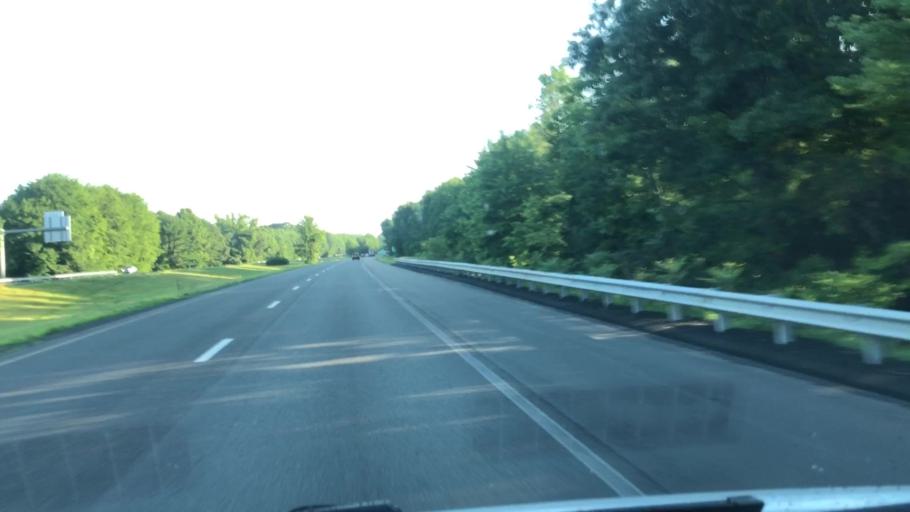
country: US
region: Massachusetts
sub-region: Franklin County
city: South Deerfield
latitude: 42.4746
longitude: -72.6168
